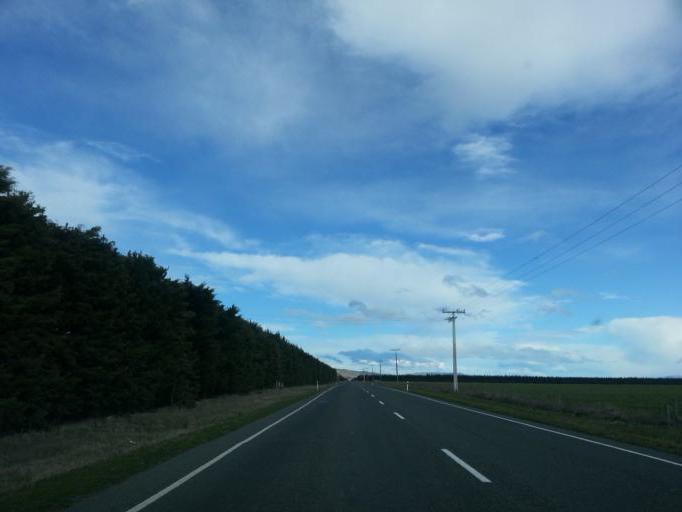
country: NZ
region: Canterbury
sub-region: Hurunui District
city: Amberley
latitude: -42.8075
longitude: 172.8213
